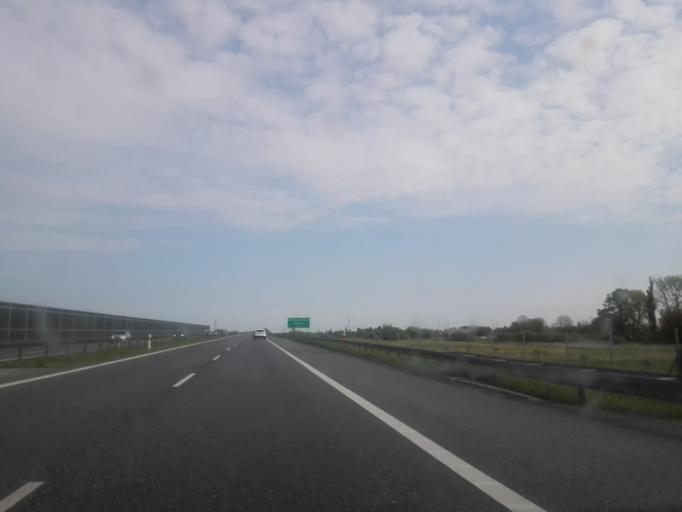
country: PL
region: Masovian Voivodeship
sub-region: Powiat zyrardowski
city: Mszczonow
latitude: 51.9620
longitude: 20.4994
